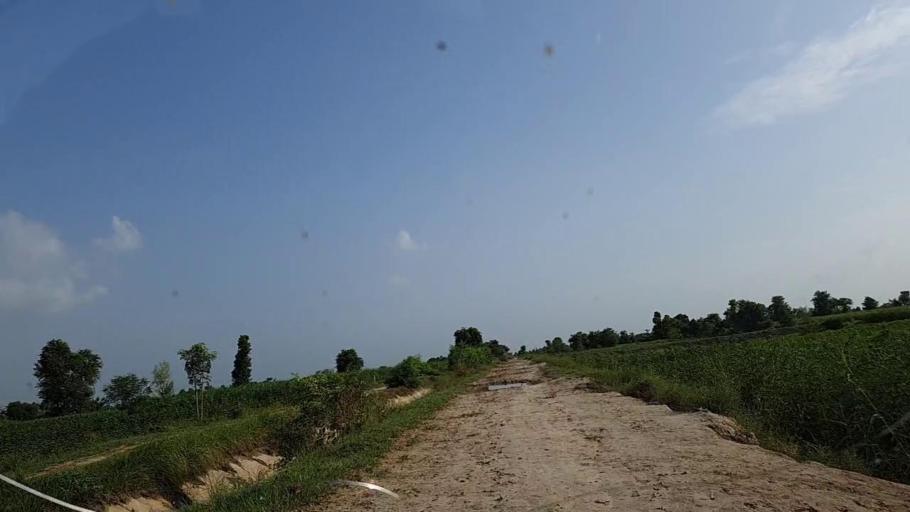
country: PK
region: Sindh
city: Bhiria
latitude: 26.8604
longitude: 68.2513
